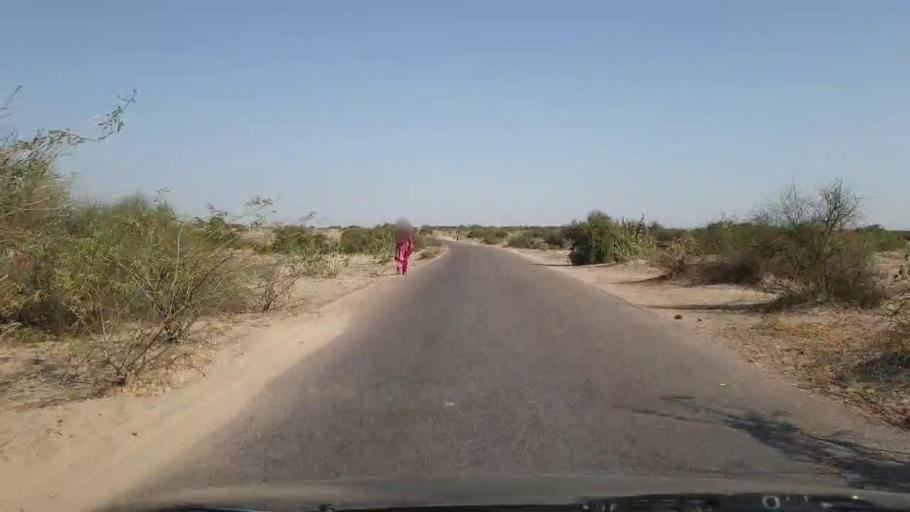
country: PK
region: Sindh
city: Chor
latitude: 25.5089
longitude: 69.8182
